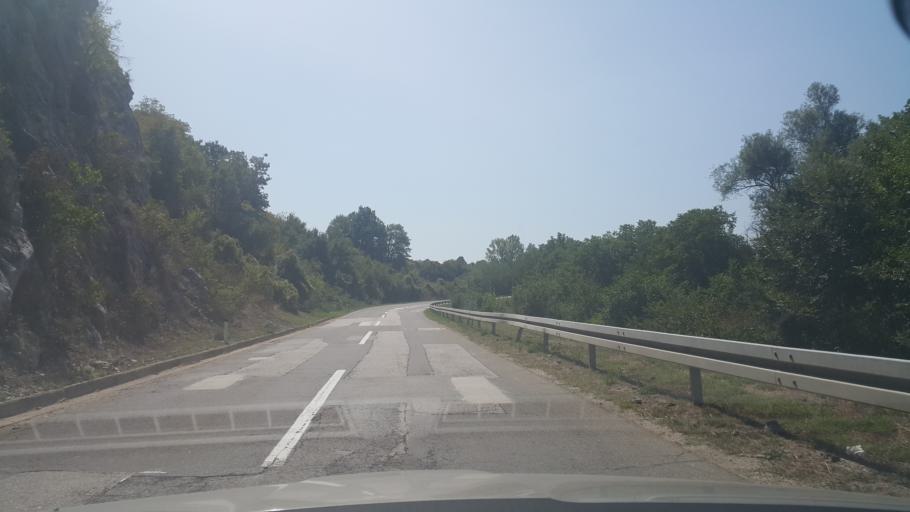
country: RS
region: Central Serbia
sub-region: Zajecarski Okrug
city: Zajecar
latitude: 43.7639
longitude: 22.3103
